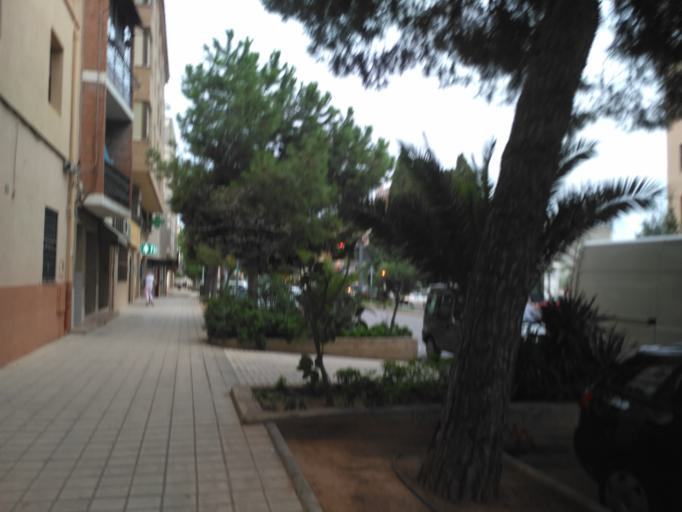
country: ES
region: Valencia
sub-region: Provincia de Castello
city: Castello de la Plana
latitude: 39.9873
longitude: -0.0608
